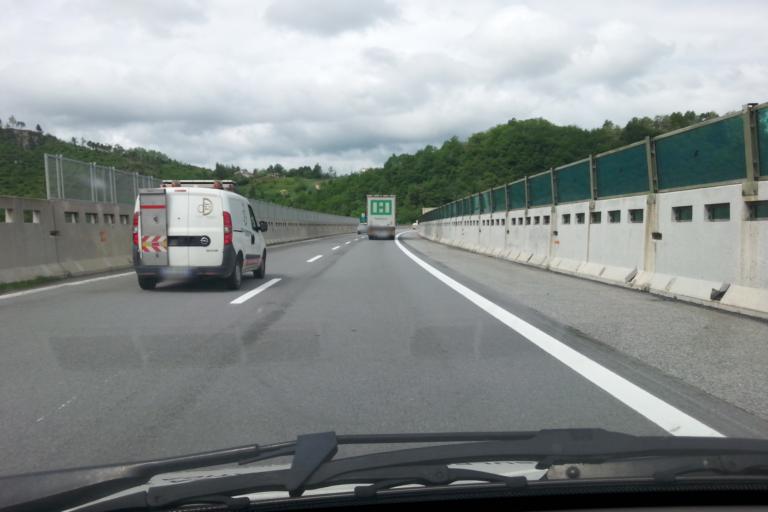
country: IT
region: Liguria
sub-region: Provincia di Savona
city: Millesimo
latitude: 44.3556
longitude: 8.2077
